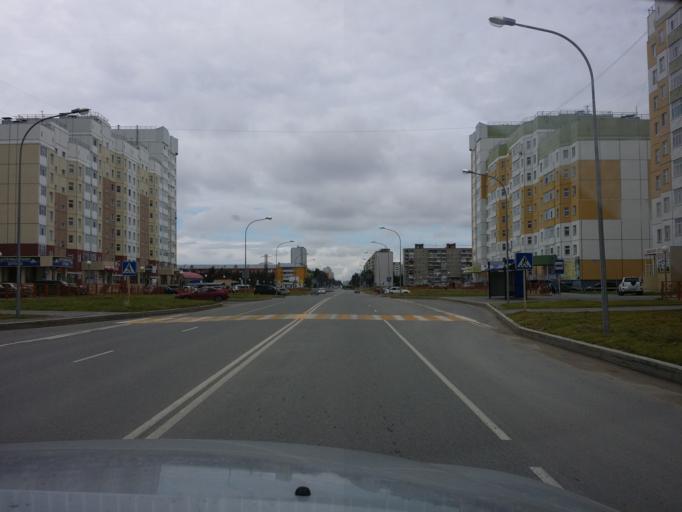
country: RU
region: Khanty-Mansiyskiy Avtonomnyy Okrug
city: Nizhnevartovsk
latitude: 60.9328
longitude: 76.6191
